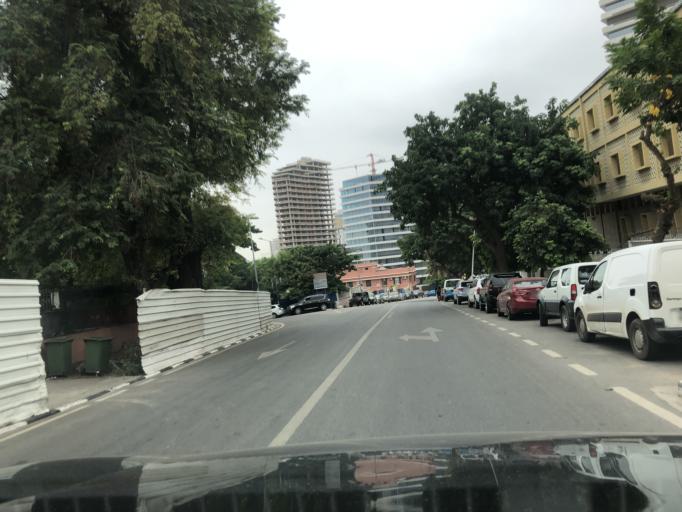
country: AO
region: Luanda
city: Luanda
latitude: -8.8166
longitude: 13.2276
